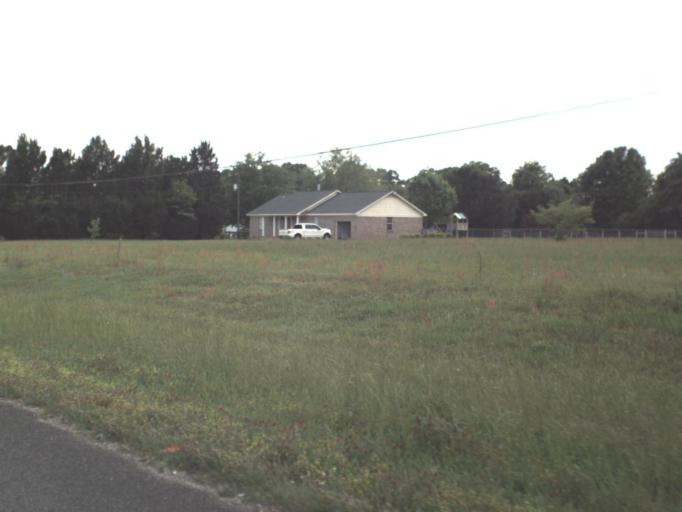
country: US
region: Florida
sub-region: Escambia County
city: Cantonment
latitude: 30.6650
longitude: -87.3516
